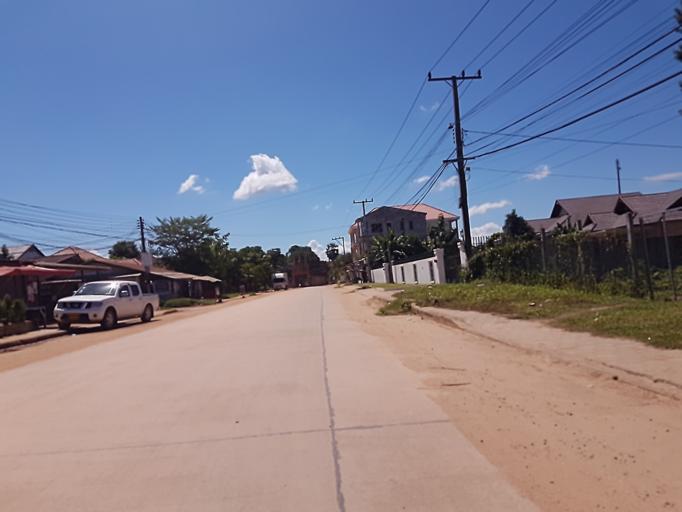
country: LA
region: Vientiane
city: Vientiane
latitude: 17.9318
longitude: 102.6345
